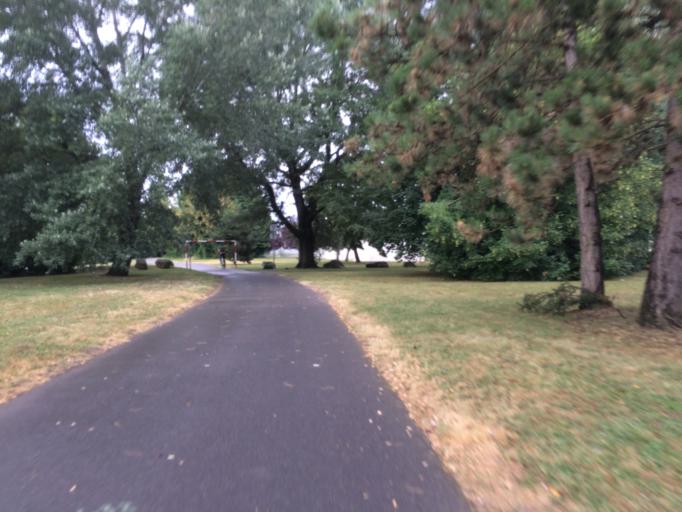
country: FR
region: Picardie
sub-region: Departement de l'Oise
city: Jaux
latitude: 49.4001
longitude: 2.7916
